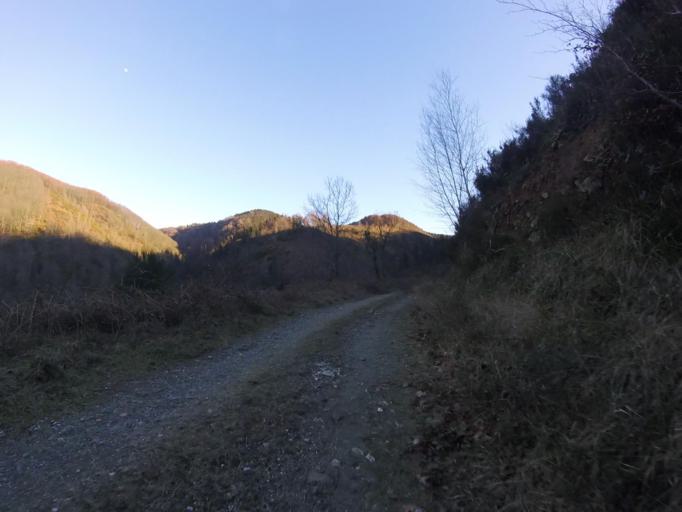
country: ES
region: Navarre
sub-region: Provincia de Navarra
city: Arano
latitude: 43.2540
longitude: -1.8442
